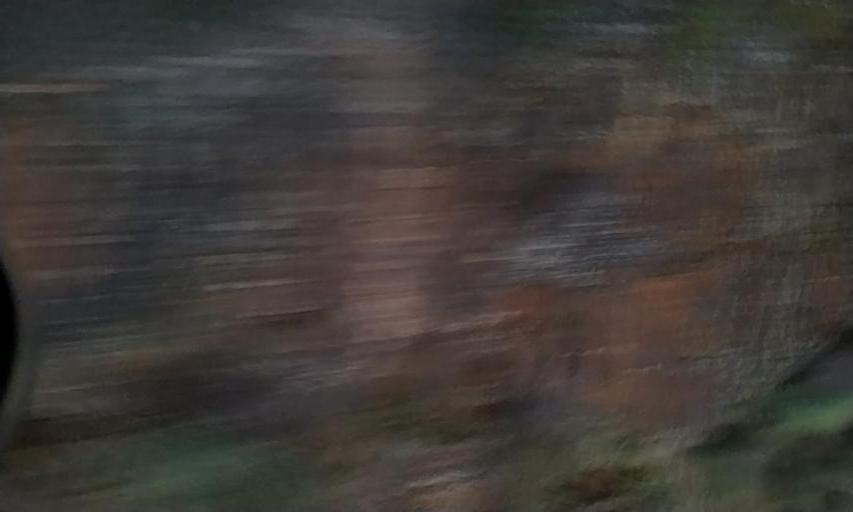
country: ES
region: Extremadura
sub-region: Provincia de Caceres
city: Piedras Albas
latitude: 39.8166
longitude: -6.9820
